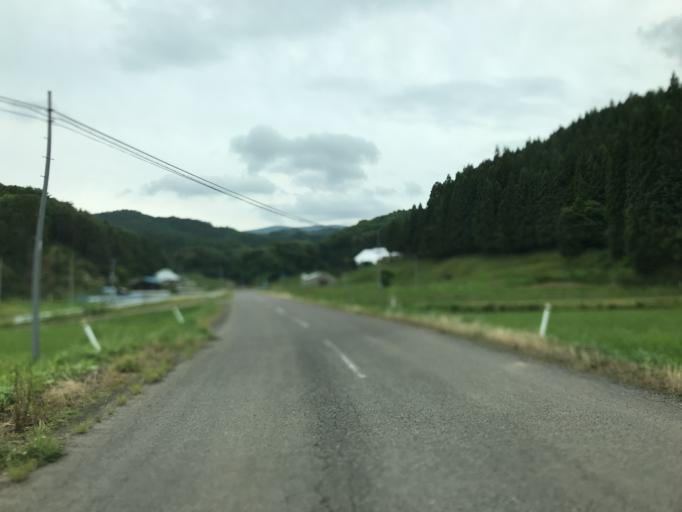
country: JP
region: Fukushima
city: Funehikimachi-funehiki
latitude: 37.3980
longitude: 140.6639
